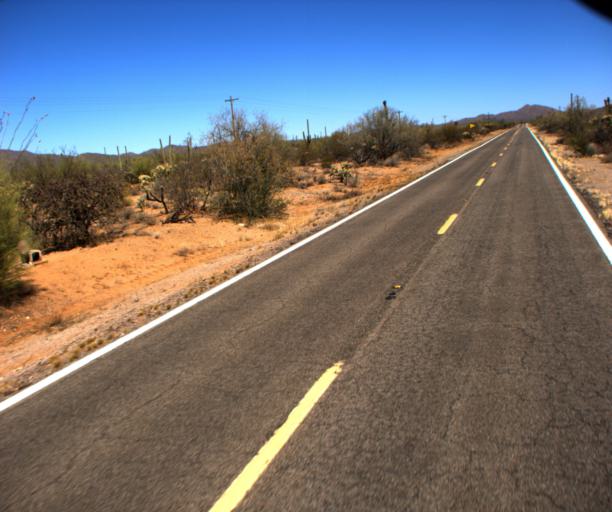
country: US
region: Arizona
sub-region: Pima County
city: Sells
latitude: 32.1320
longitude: -112.0911
